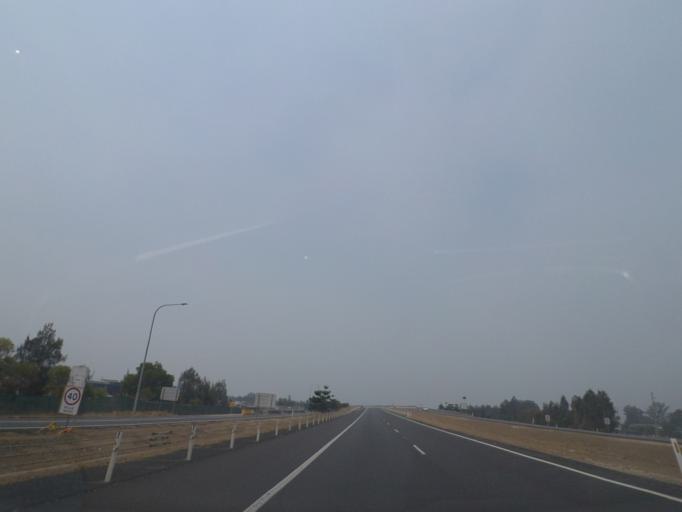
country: AU
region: New South Wales
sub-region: Ballina
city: Ballina
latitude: -28.8625
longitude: 153.5158
